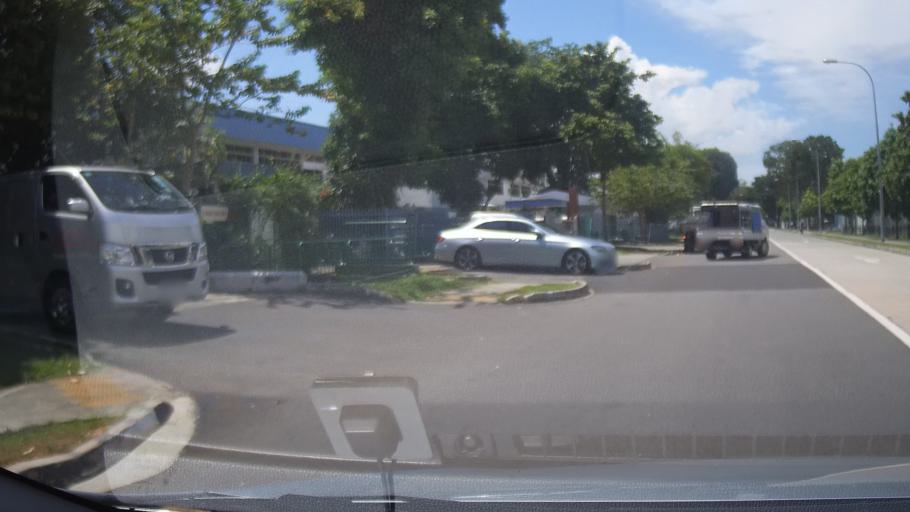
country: MY
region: Johor
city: Johor Bahru
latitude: 1.3321
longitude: 103.6956
